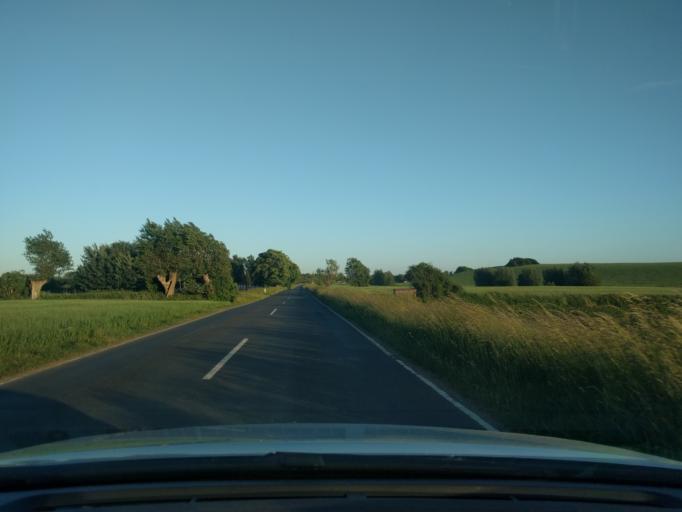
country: DK
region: South Denmark
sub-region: Kerteminde Kommune
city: Kerteminde
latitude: 55.5598
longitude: 10.6508
